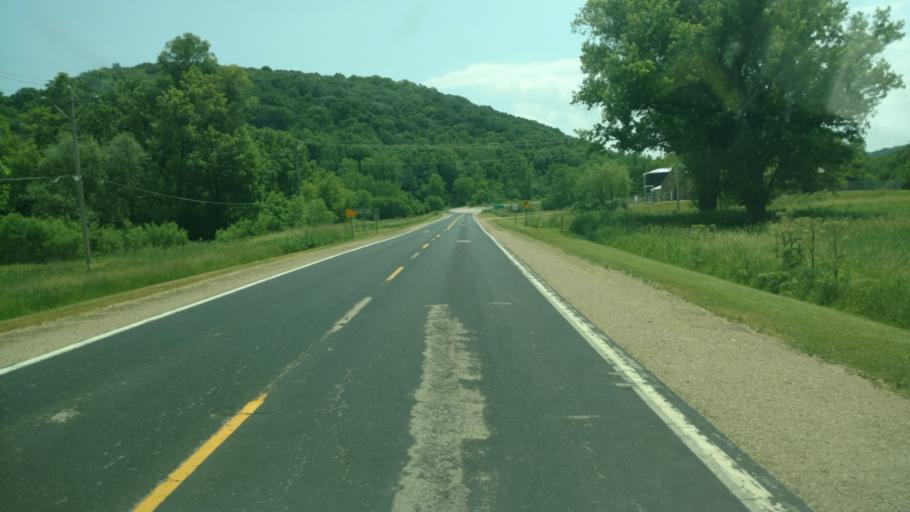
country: US
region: Wisconsin
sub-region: Monroe County
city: Cashton
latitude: 43.5698
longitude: -90.6364
